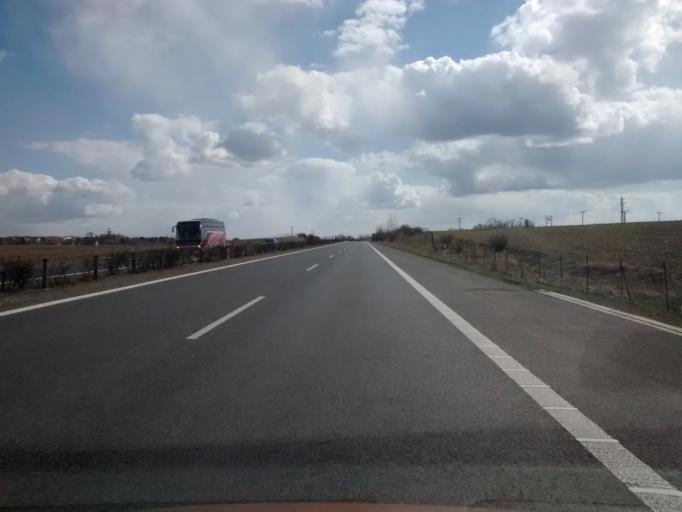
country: CZ
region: Central Bohemia
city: Velvary
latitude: 50.3467
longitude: 14.2783
